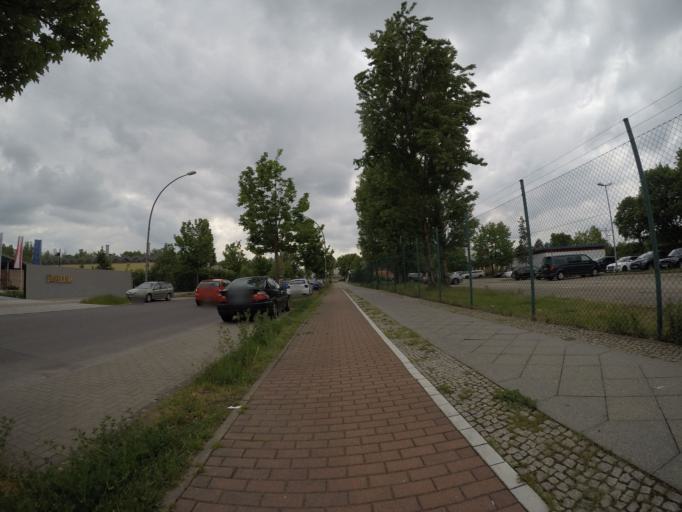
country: DE
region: Berlin
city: Falkenberg
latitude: 52.5459
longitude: 13.5368
